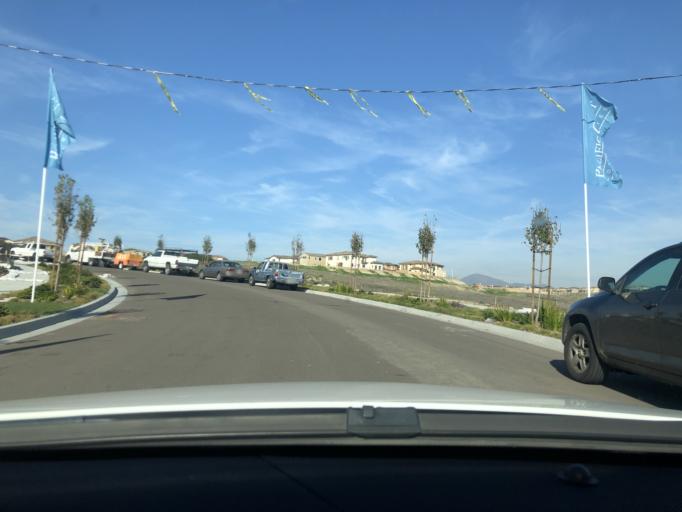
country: US
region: California
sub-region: San Diego County
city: Bonita
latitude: 32.6079
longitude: -116.9910
